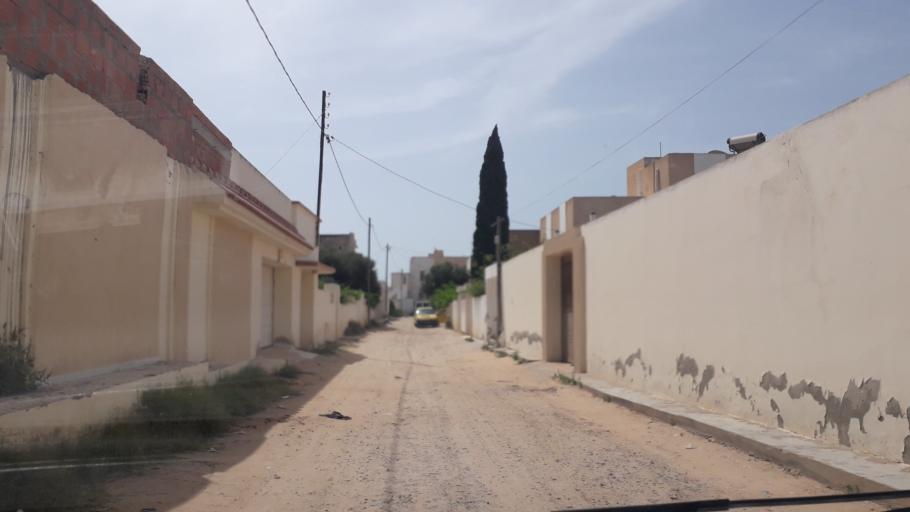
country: TN
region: Safaqis
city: Al Qarmadah
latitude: 34.8010
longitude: 10.7721
